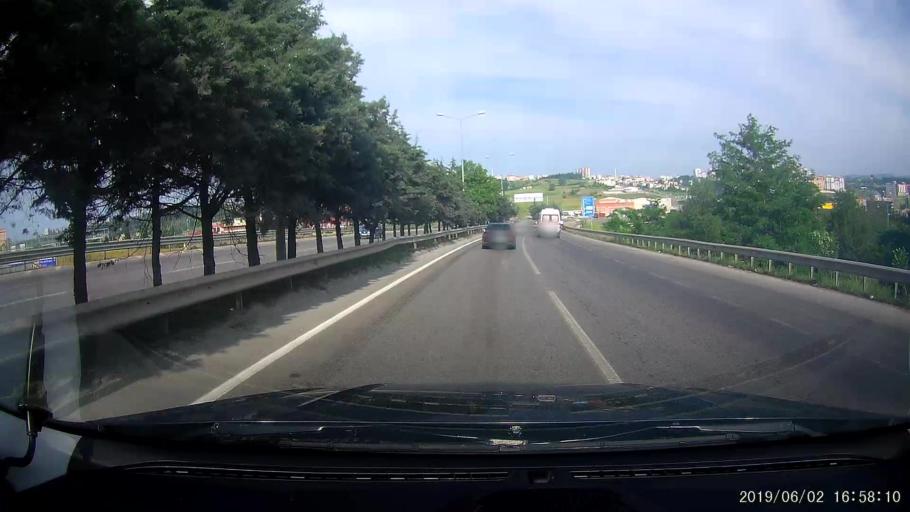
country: TR
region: Samsun
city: Samsun
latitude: 41.2904
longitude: 36.2863
